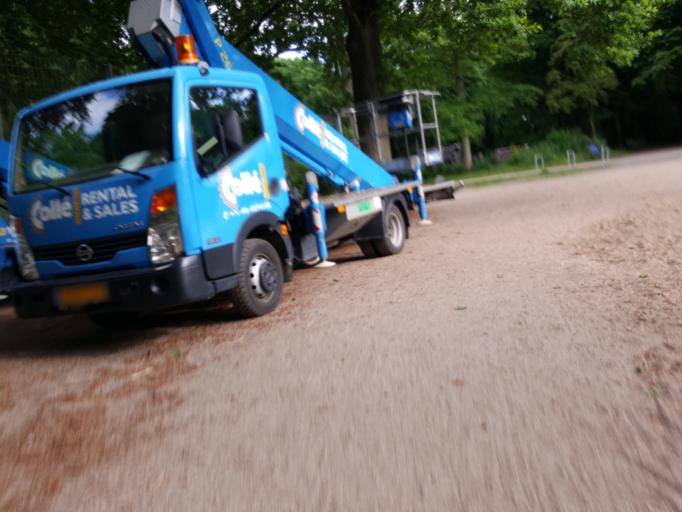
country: DE
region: Hamburg
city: Marienthal
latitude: 53.5570
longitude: 10.0616
